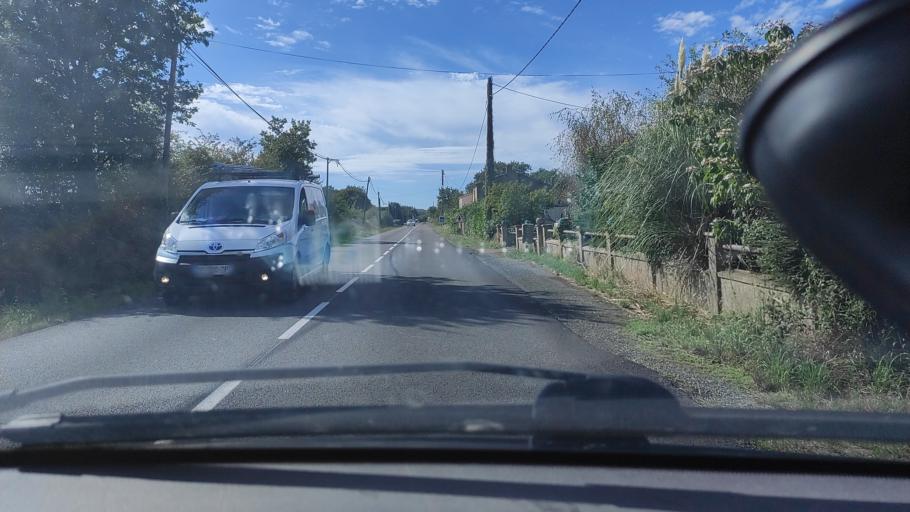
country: FR
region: Pays de la Loire
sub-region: Departement de la Vendee
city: La Boissiere-des-Landes
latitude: 46.5572
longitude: -1.4416
